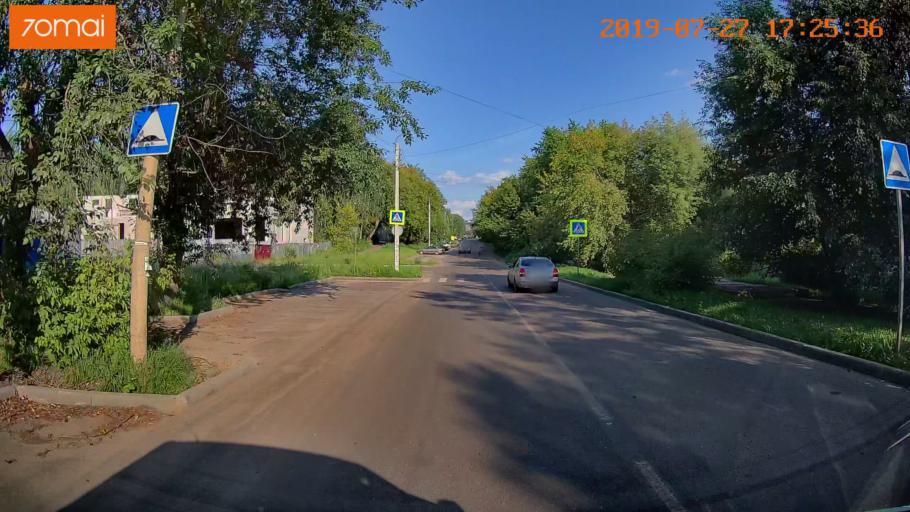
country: RU
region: Ivanovo
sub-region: Gorod Ivanovo
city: Ivanovo
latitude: 57.0168
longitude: 40.9609
